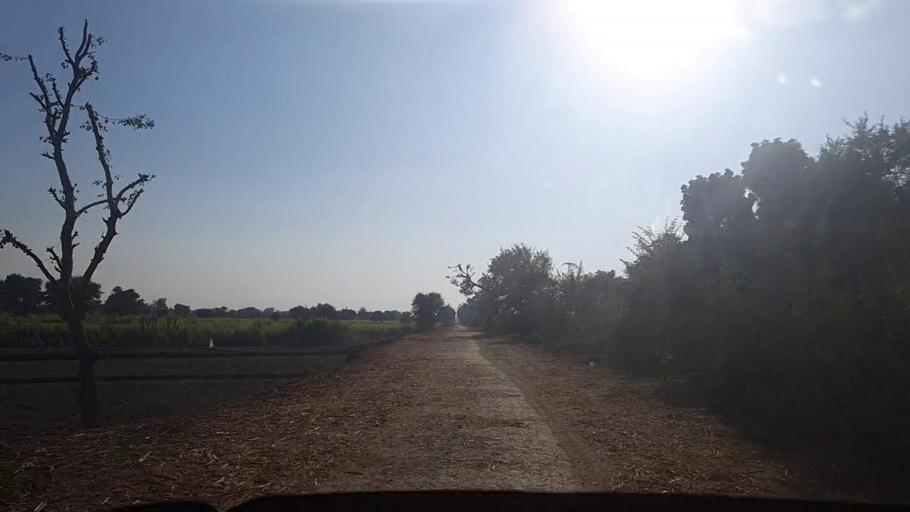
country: PK
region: Sindh
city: Gambat
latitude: 27.3538
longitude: 68.4533
